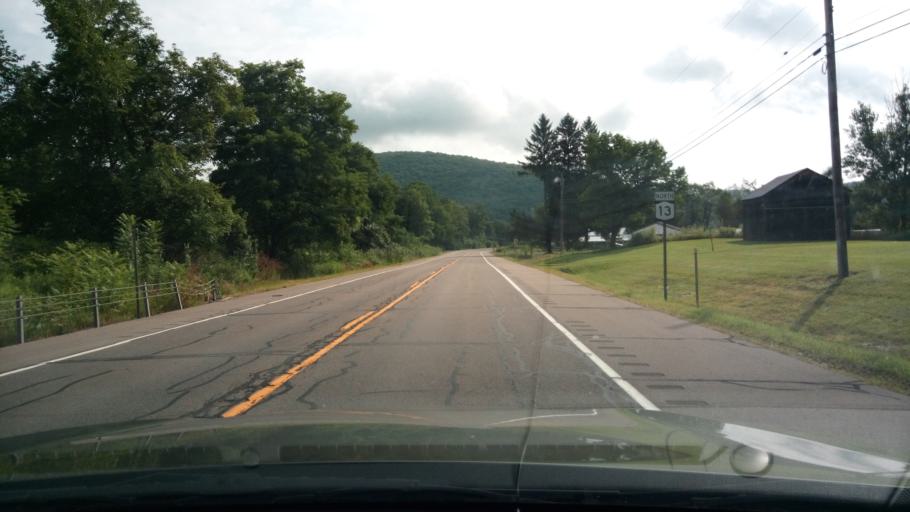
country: US
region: New York
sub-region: Chemung County
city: Horseheads North
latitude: 42.2929
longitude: -76.7234
